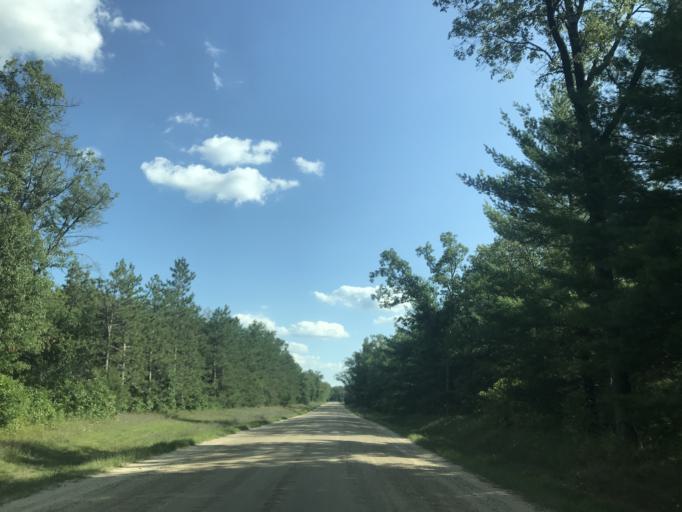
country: US
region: Michigan
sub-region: Newaygo County
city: Newaygo
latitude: 43.4425
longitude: -85.7326
